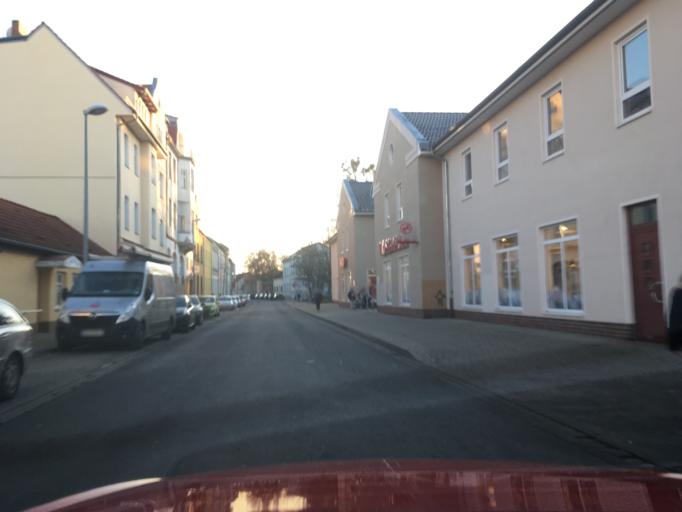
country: DE
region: Saxony-Anhalt
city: Rosslau
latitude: 51.8889
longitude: 12.2463
